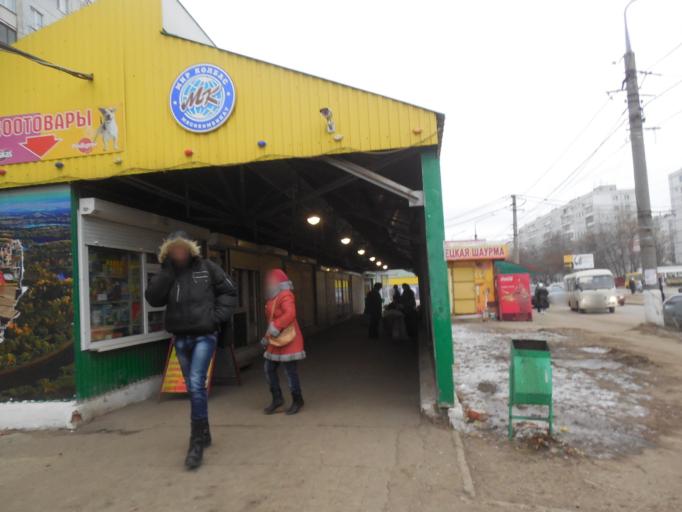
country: RU
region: Samara
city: Samara
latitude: 53.2389
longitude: 50.2157
